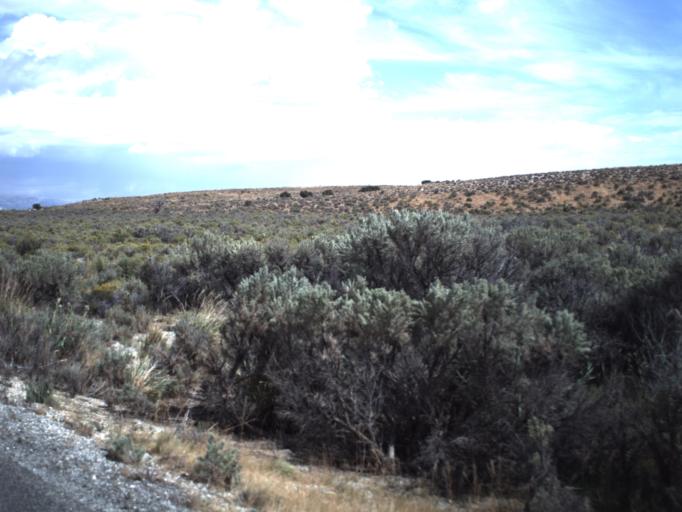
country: US
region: Idaho
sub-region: Cassia County
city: Burley
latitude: 41.6823
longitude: -113.5401
